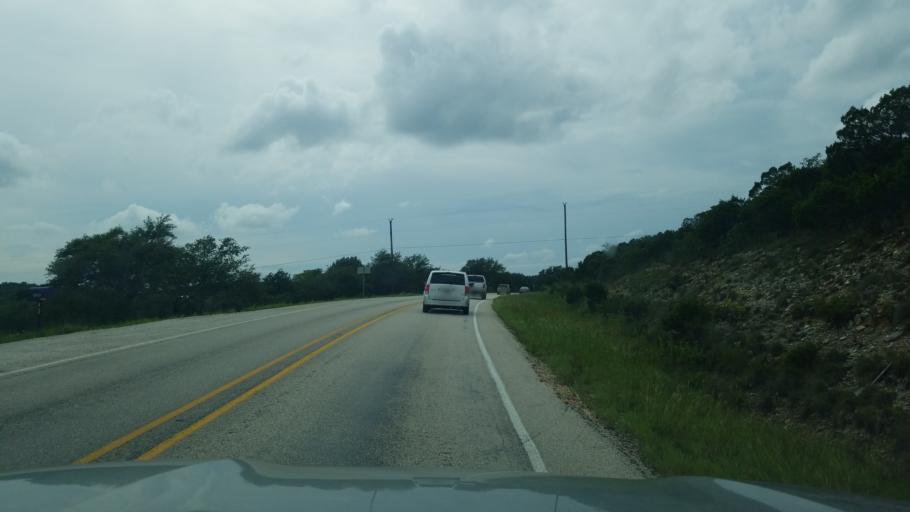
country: US
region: Texas
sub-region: Blanco County
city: Blanco
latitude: 30.1408
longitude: -98.2654
